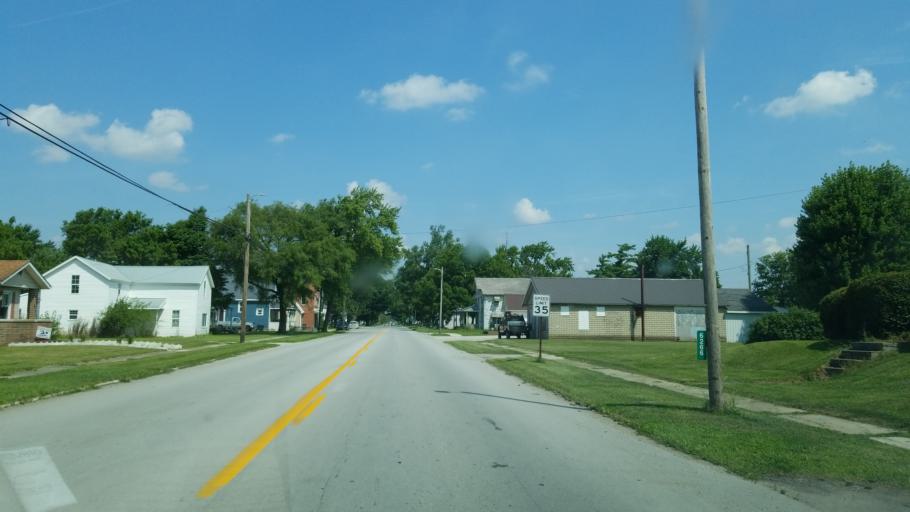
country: US
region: Ohio
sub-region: Seneca County
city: Fostoria
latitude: 41.2422
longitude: -83.4901
